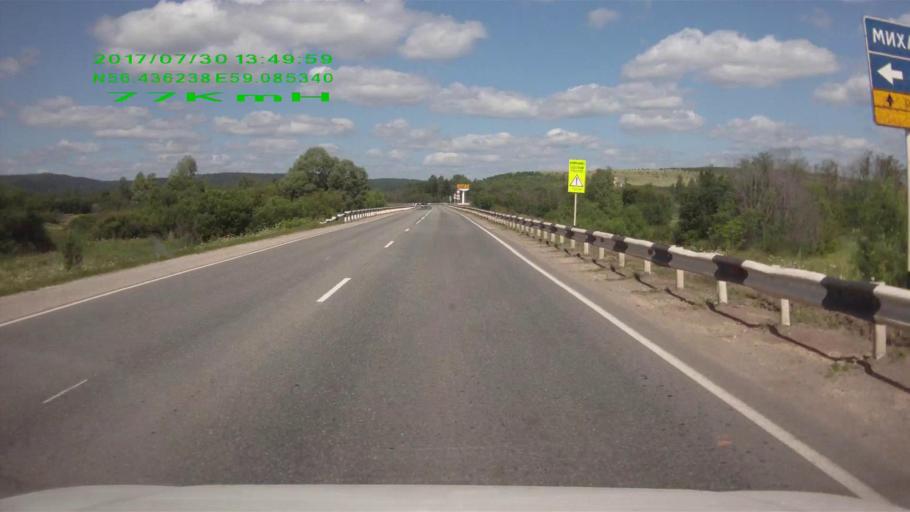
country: RU
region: Sverdlovsk
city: Mikhaylovsk
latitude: 56.4368
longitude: 59.0856
